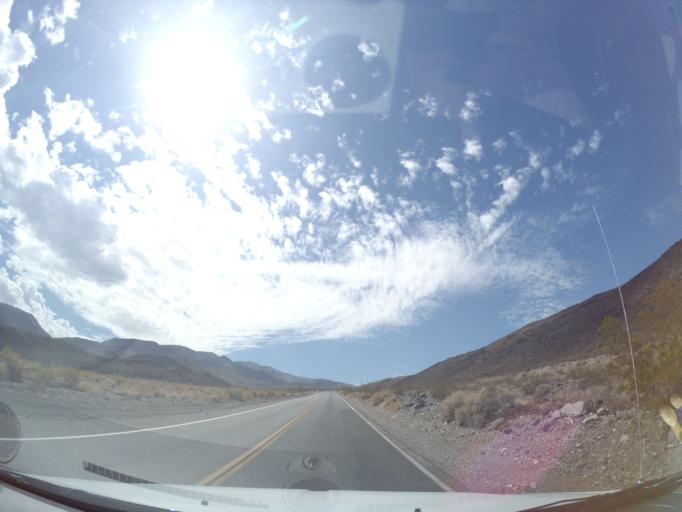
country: US
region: Nevada
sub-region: Nye County
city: Beatty
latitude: 36.4620
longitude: -117.2367
